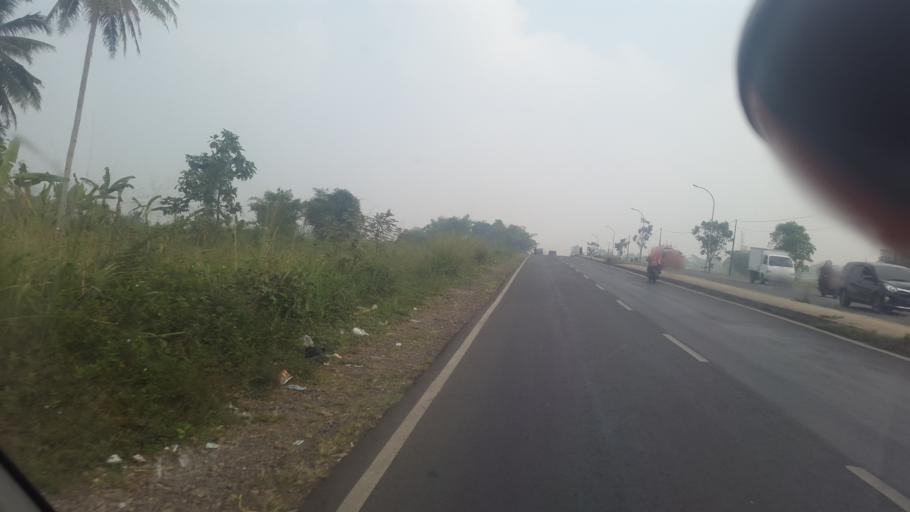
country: ID
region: West Java
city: Sukabumi
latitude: -6.9206
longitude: 106.8892
